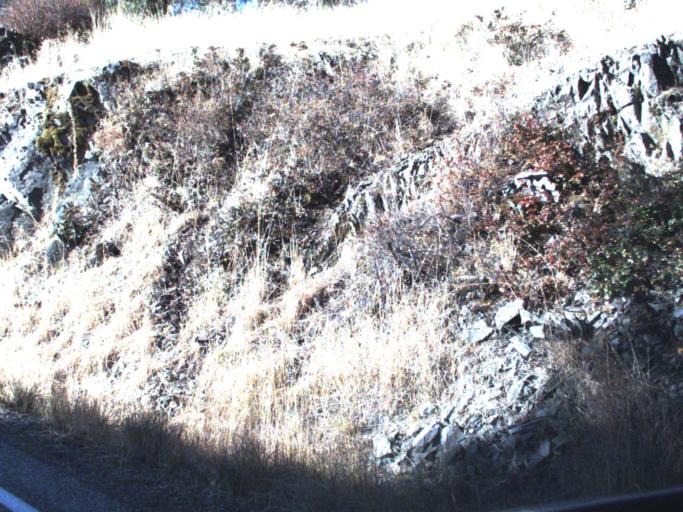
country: CA
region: British Columbia
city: Grand Forks
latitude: 48.9457
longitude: -118.5539
